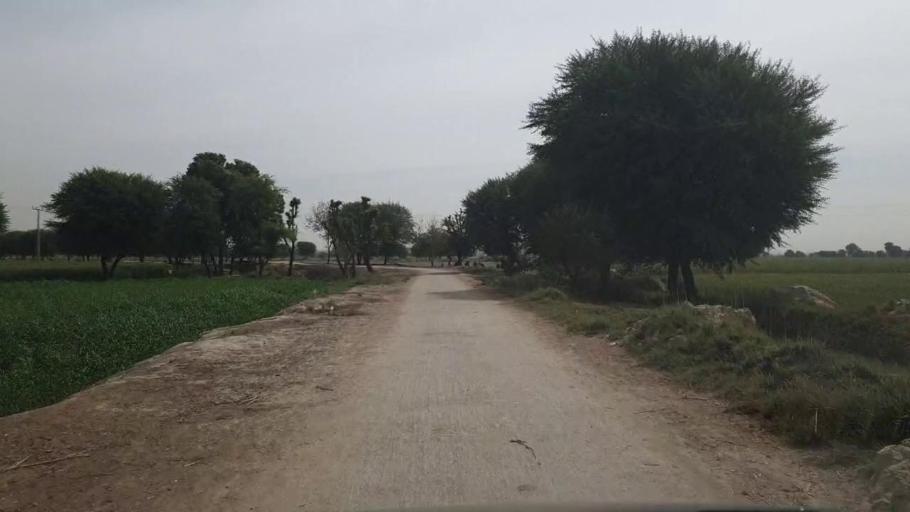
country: PK
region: Sindh
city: Umarkot
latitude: 25.2325
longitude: 69.6979
